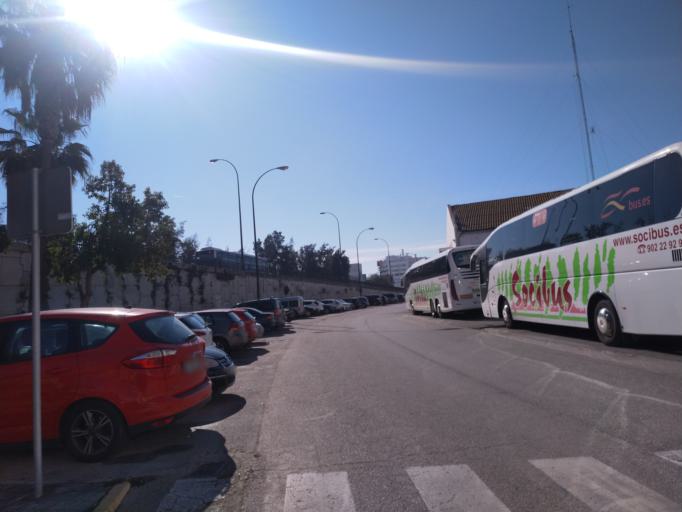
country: ES
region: Andalusia
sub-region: Provincia de Cadiz
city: San Fernando
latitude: 36.4717
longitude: -6.1896
